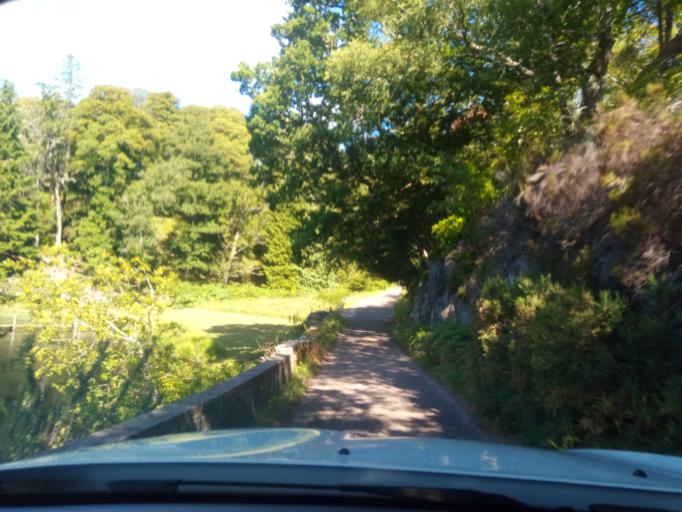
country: GB
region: Scotland
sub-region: Argyll and Bute
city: Isle Of Mull
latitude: 56.7566
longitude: -5.8072
